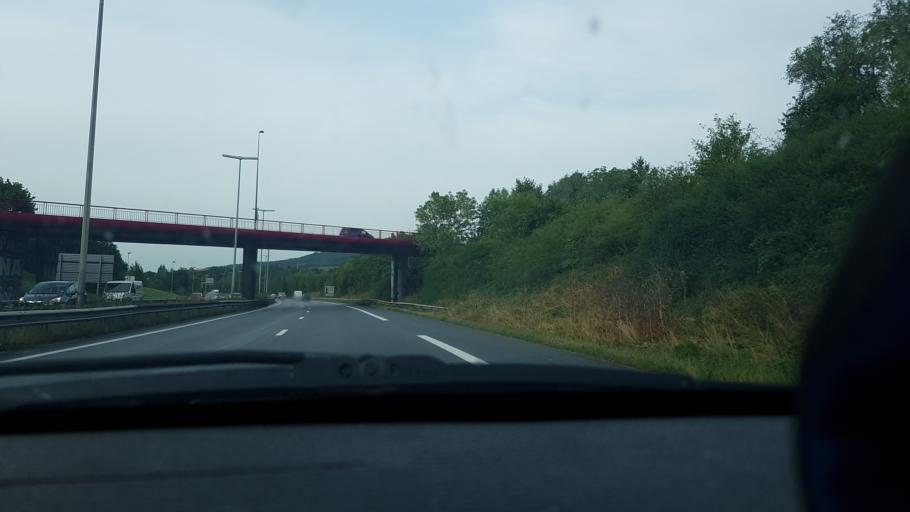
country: FR
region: Lorraine
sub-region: Departement de Meurthe-et-Moselle
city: Vandoeuvre-les-Nancy
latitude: 48.6532
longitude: 6.1824
